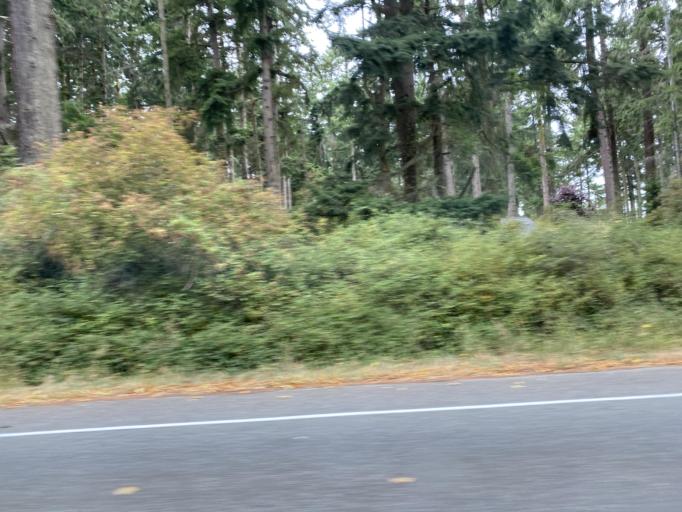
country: US
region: Washington
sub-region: Island County
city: Coupeville
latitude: 48.2209
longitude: -122.6511
